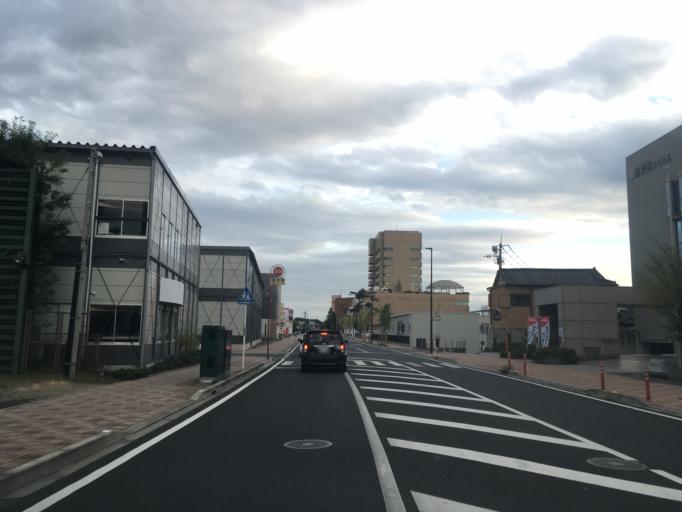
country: JP
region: Gunma
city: Maebashi-shi
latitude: 36.3898
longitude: 139.0595
